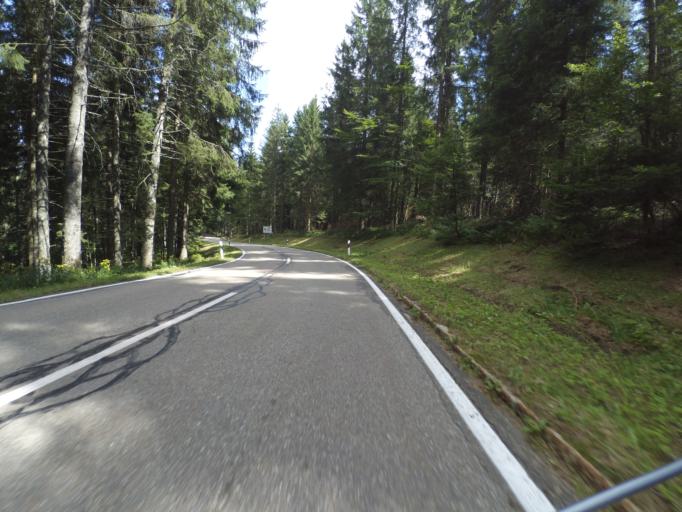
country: DE
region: Baden-Wuerttemberg
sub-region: Freiburg Region
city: Sankt Peter
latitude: 48.0591
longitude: 8.0238
